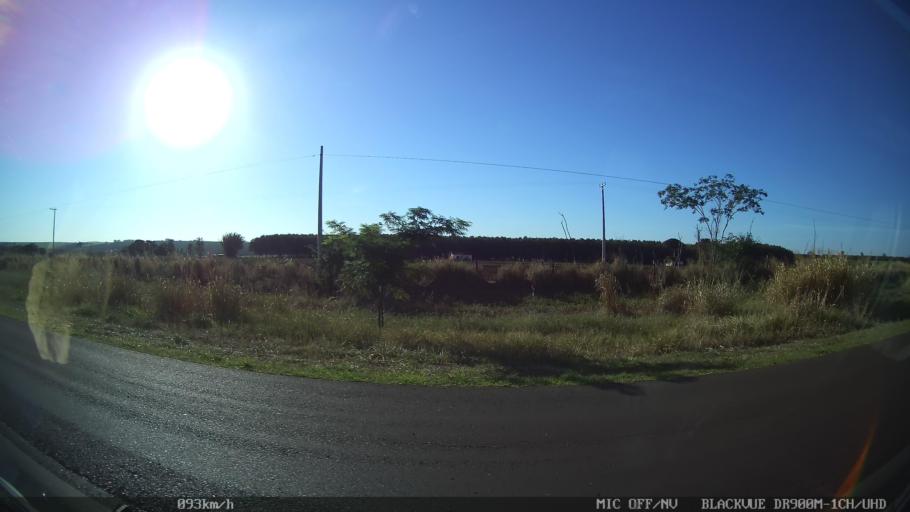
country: BR
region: Sao Paulo
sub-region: Guapiacu
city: Guapiacu
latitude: -20.7514
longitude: -49.1384
